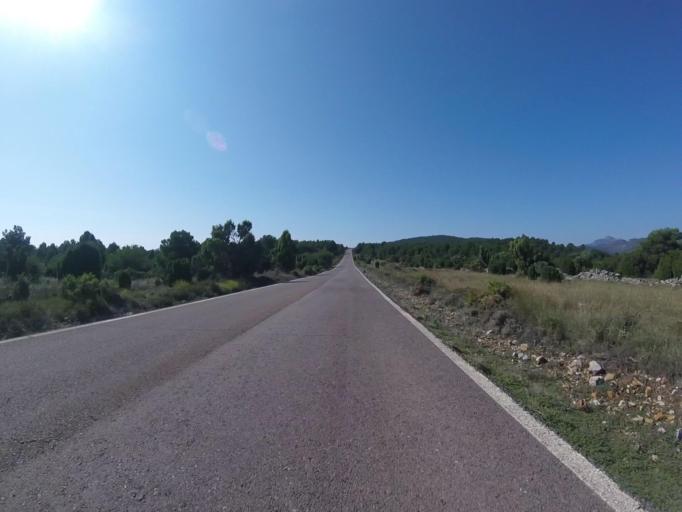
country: ES
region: Valencia
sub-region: Provincia de Castello
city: Benafigos
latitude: 40.2854
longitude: -0.2384
